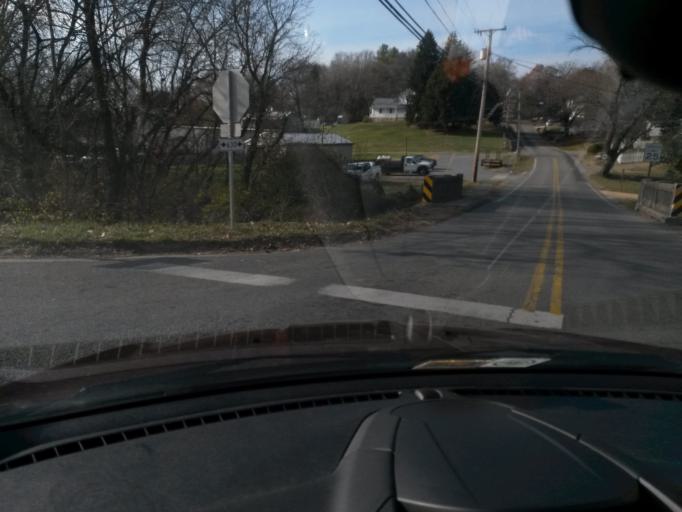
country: US
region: Virginia
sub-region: Botetourt County
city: Fincastle
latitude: 37.4988
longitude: -79.8795
